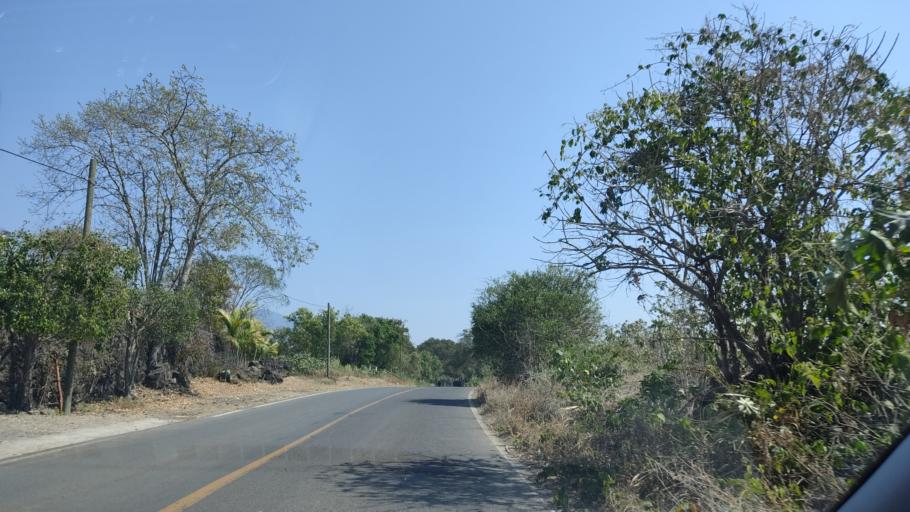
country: MX
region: Nayarit
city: Puga
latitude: 21.5339
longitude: -104.8088
